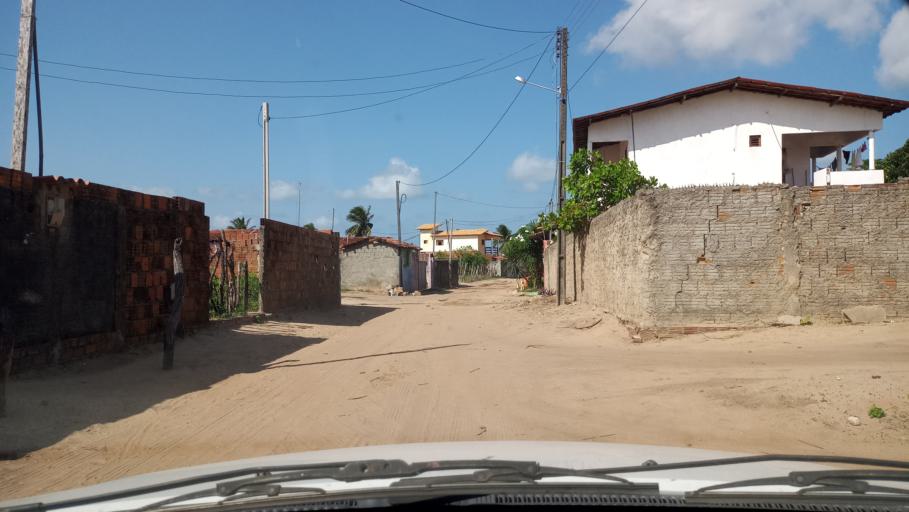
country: BR
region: Rio Grande do Norte
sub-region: Ares
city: Ares
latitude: -6.2158
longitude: -35.1097
